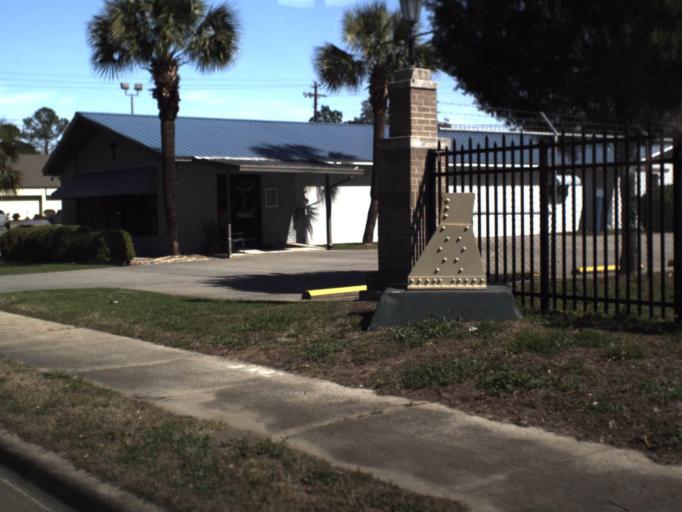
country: US
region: Florida
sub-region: Bay County
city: Lynn Haven
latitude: 30.2418
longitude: -85.6487
